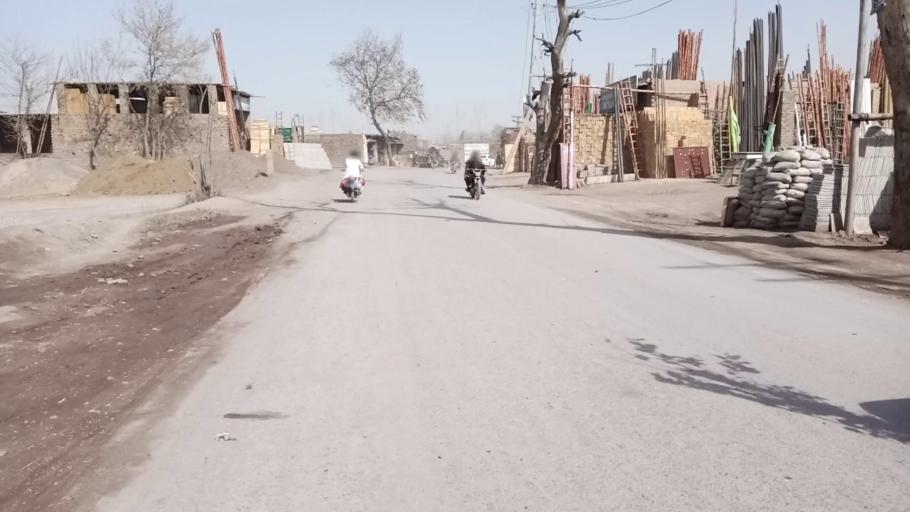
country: PK
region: Khyber Pakhtunkhwa
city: Peshawar
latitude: 33.9964
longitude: 71.6339
